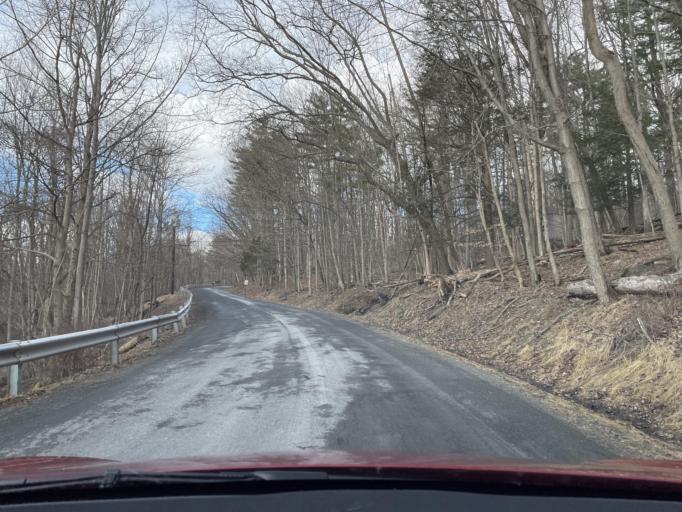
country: US
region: New York
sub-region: Ulster County
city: Woodstock
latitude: 42.0554
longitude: -74.1355
